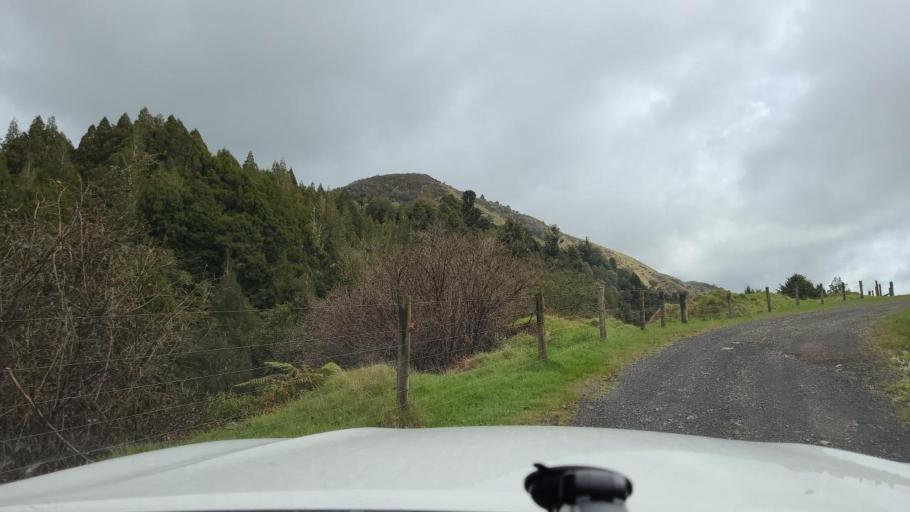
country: NZ
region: Bay of Plenty
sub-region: Opotiki District
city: Opotiki
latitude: -38.2265
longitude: 177.6136
